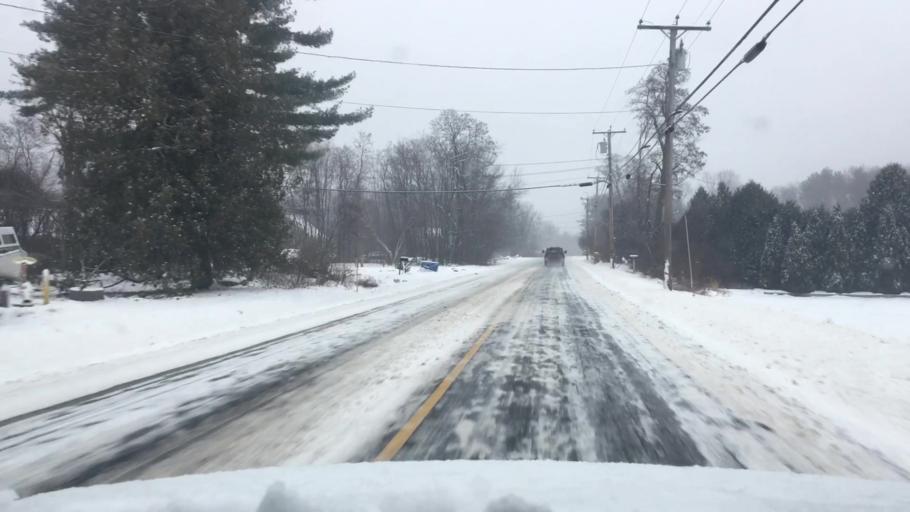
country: US
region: Maine
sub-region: Cumberland County
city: Cumberland Center
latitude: 43.8455
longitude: -70.3218
